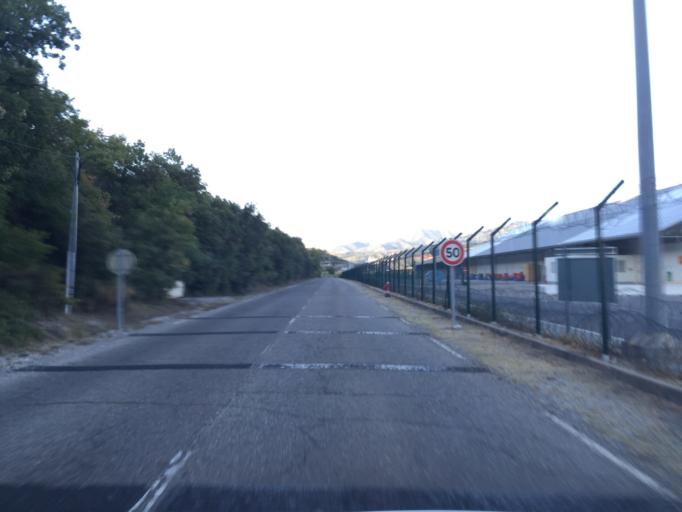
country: FR
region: Provence-Alpes-Cote d'Azur
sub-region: Departement des Alpes-de-Haute-Provence
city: Malijai
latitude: 44.0690
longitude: 5.9994
